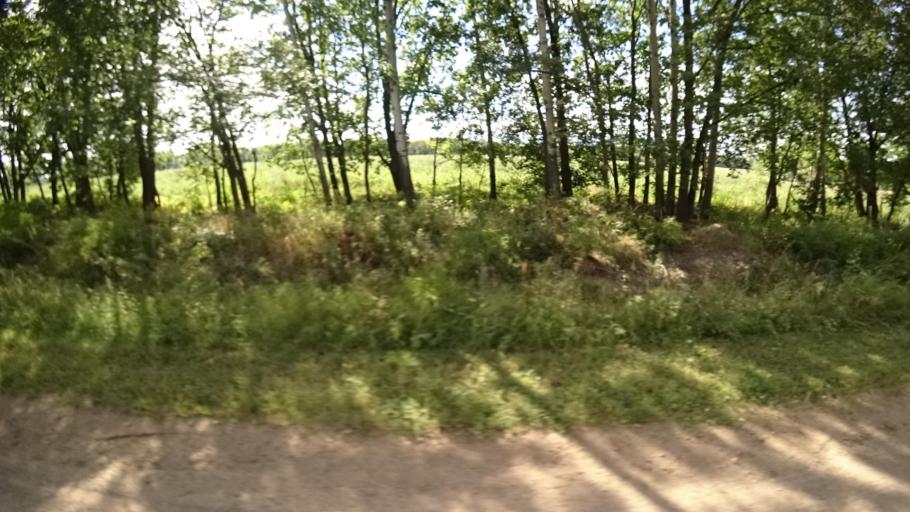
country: RU
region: Primorskiy
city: Yakovlevka
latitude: 44.4179
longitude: 133.5709
